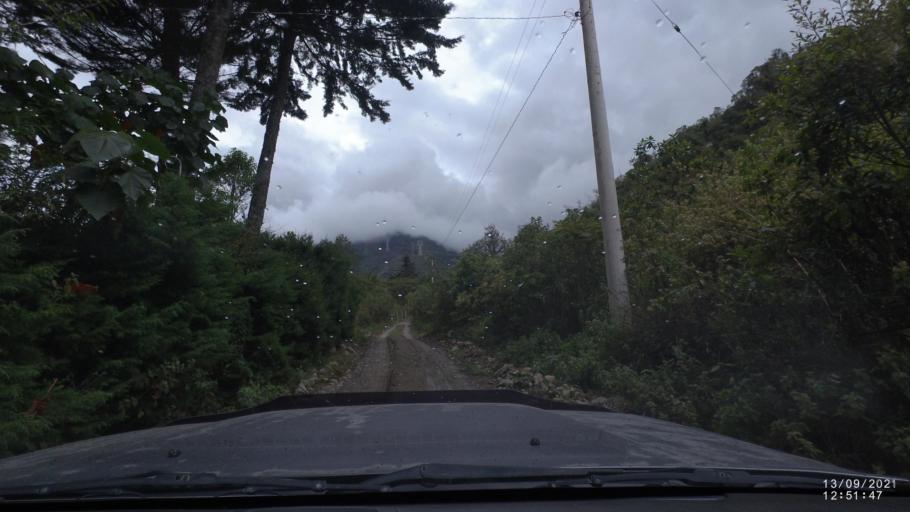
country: BO
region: Cochabamba
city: Colomi
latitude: -17.2411
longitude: -65.8211
